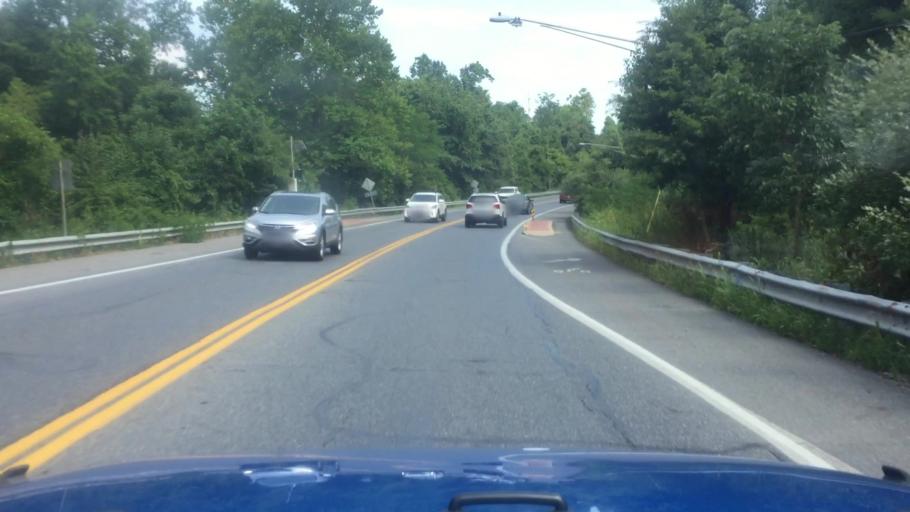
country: US
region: Maryland
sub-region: Anne Arundel County
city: Gambrills
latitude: 39.0474
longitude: -76.6871
